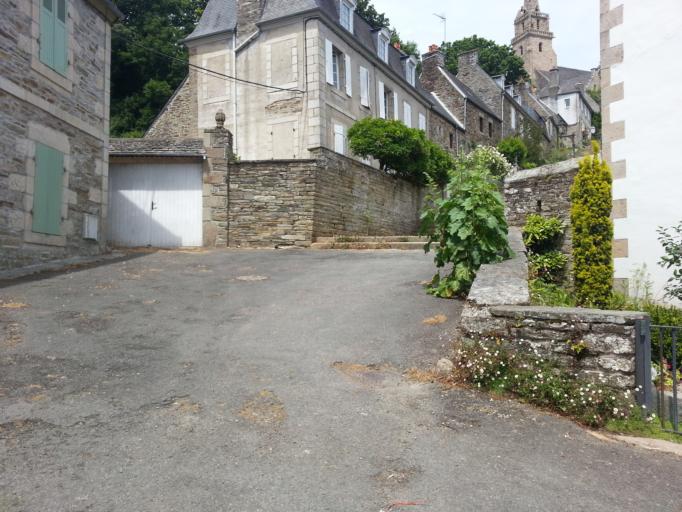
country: FR
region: Brittany
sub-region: Departement des Cotes-d'Armor
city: Lannion
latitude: 48.7348
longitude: -3.4594
